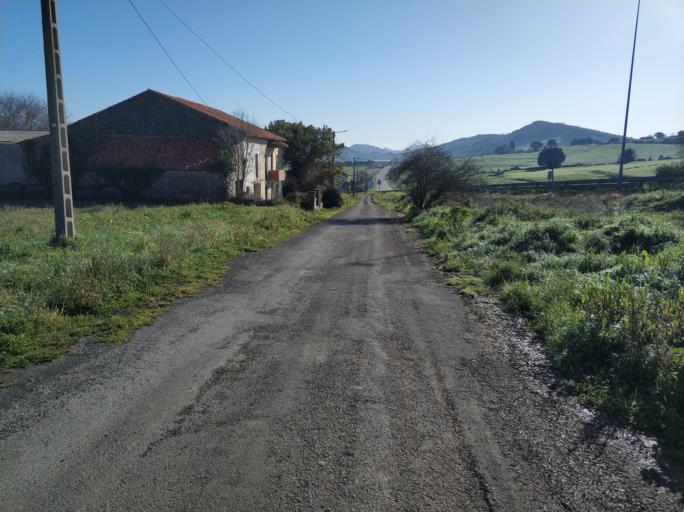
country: ES
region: Cantabria
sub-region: Provincia de Cantabria
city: Bareyo
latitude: 43.4752
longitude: -3.6059
